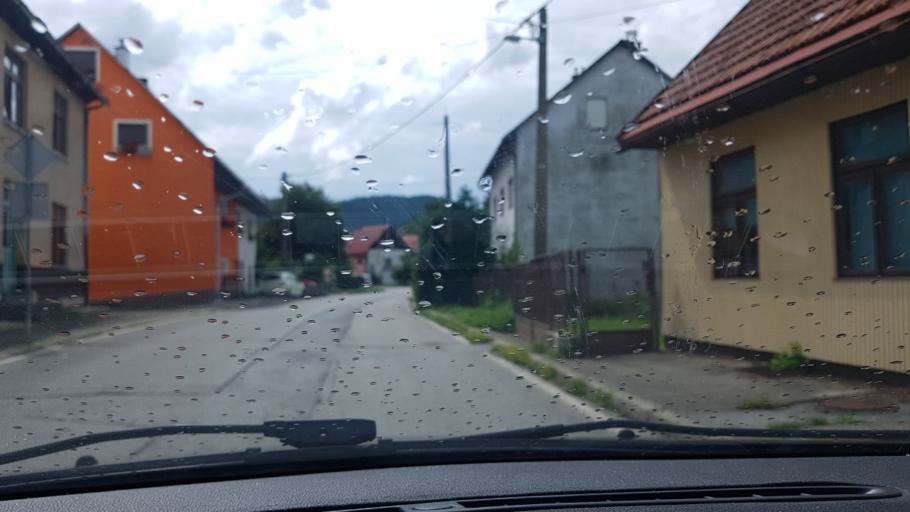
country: HR
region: Primorsko-Goranska
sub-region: Grad Delnice
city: Delnice
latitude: 45.3578
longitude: 14.7510
